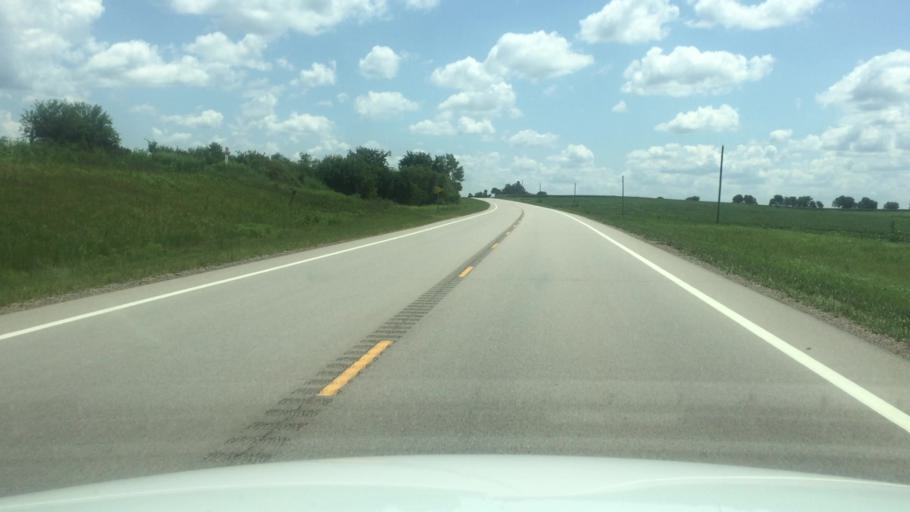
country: US
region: Kansas
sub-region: Brown County
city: Horton
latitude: 39.6134
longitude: -95.3467
